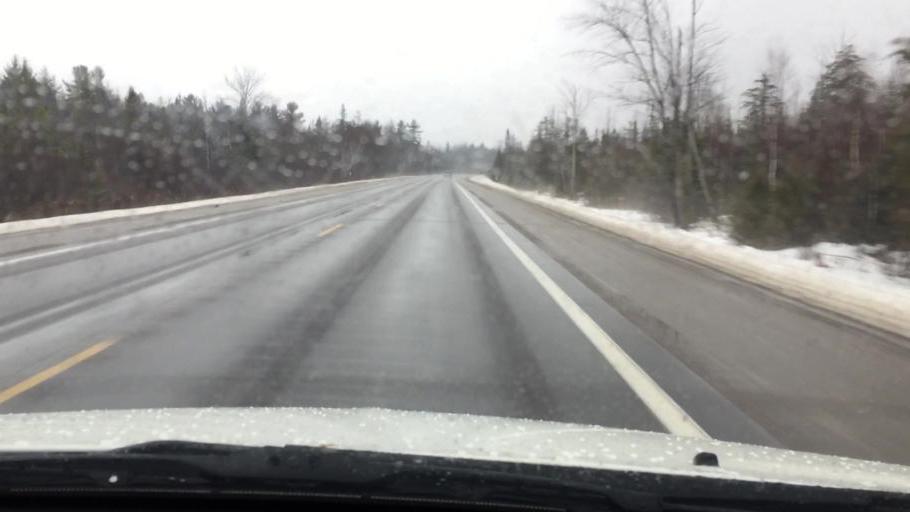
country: US
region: Michigan
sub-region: Kalkaska County
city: Kalkaska
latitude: 44.7046
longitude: -85.2001
